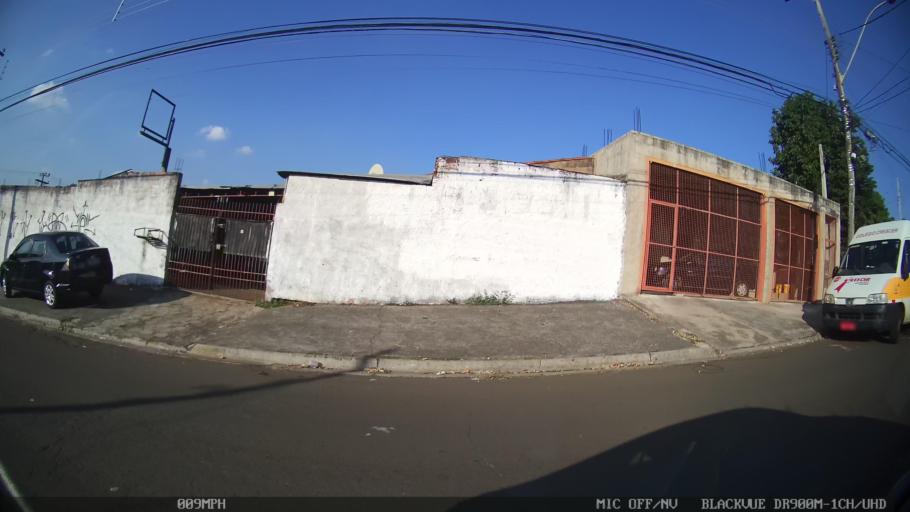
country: BR
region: Sao Paulo
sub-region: Campinas
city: Campinas
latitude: -22.9660
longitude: -47.1257
